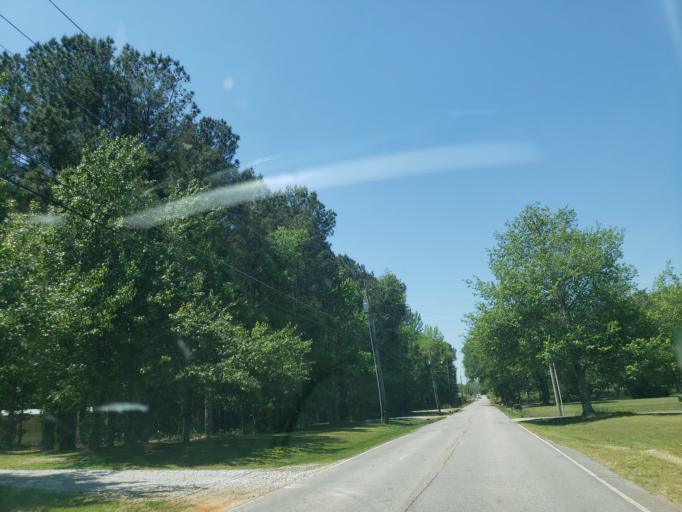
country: US
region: Alabama
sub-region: Madison County
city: Hazel Green
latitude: 34.9623
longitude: -86.6881
